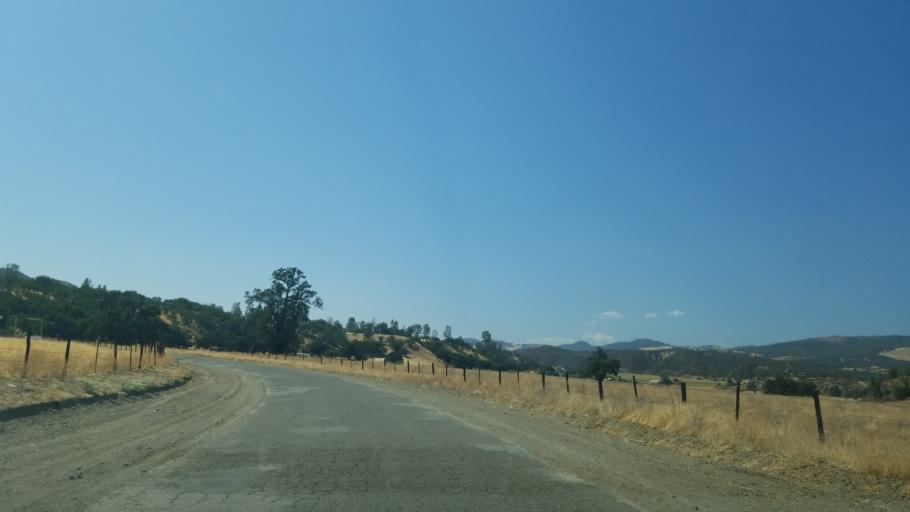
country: US
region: California
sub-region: Fresno County
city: Coalinga
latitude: 35.9091
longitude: -120.4349
